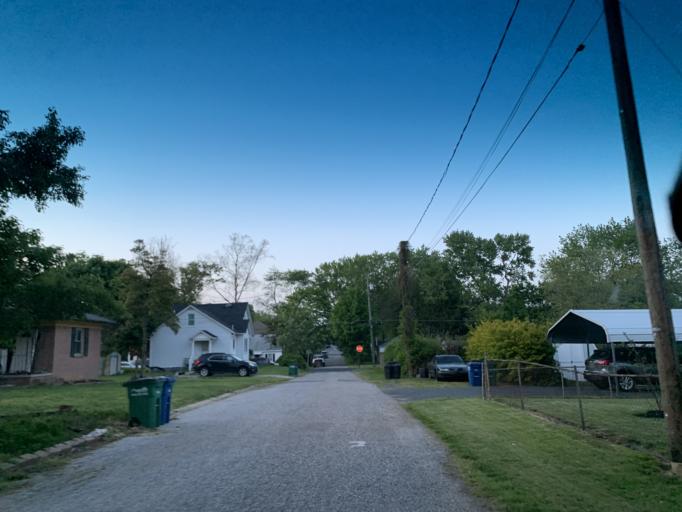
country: US
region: Maryland
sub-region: Harford County
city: Aberdeen
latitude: 39.5064
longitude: -76.1739
